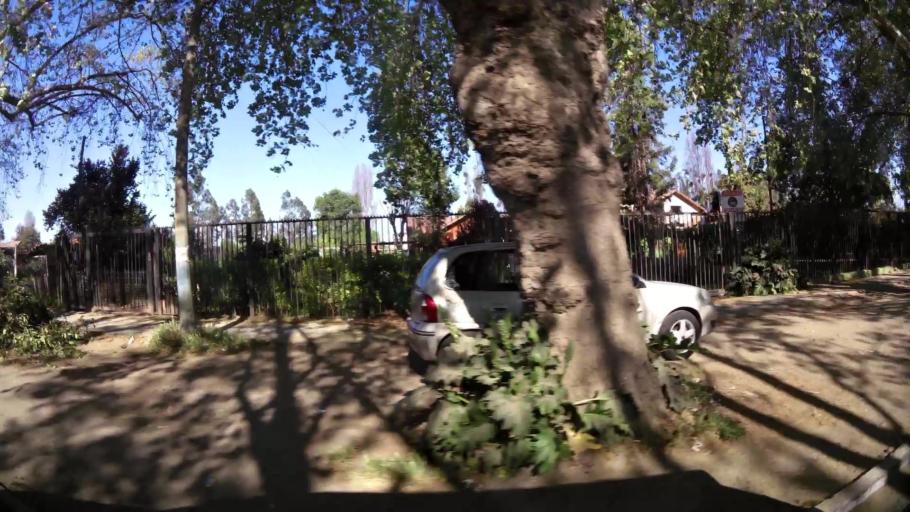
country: CL
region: Santiago Metropolitan
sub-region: Provincia de Talagante
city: Penaflor
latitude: -33.6027
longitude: -70.8690
